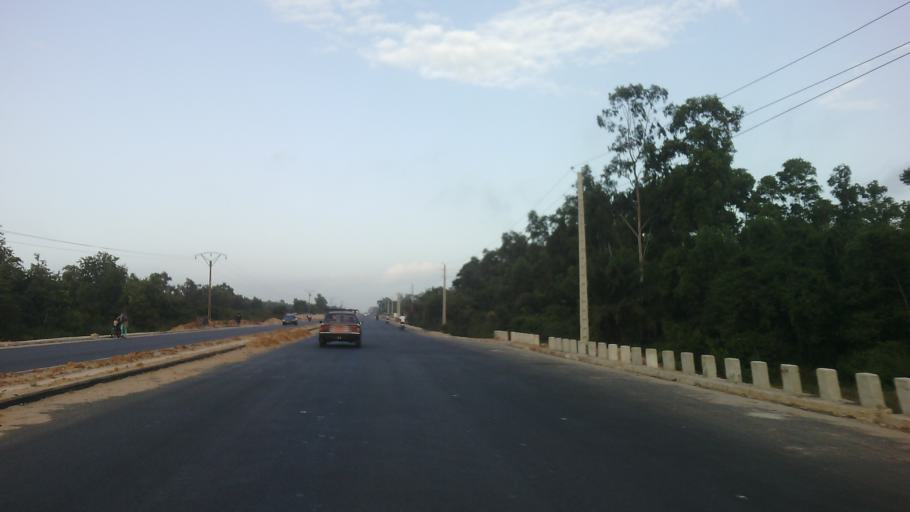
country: BJ
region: Atlantique
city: Ouidah
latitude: 6.3803
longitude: 2.1663
